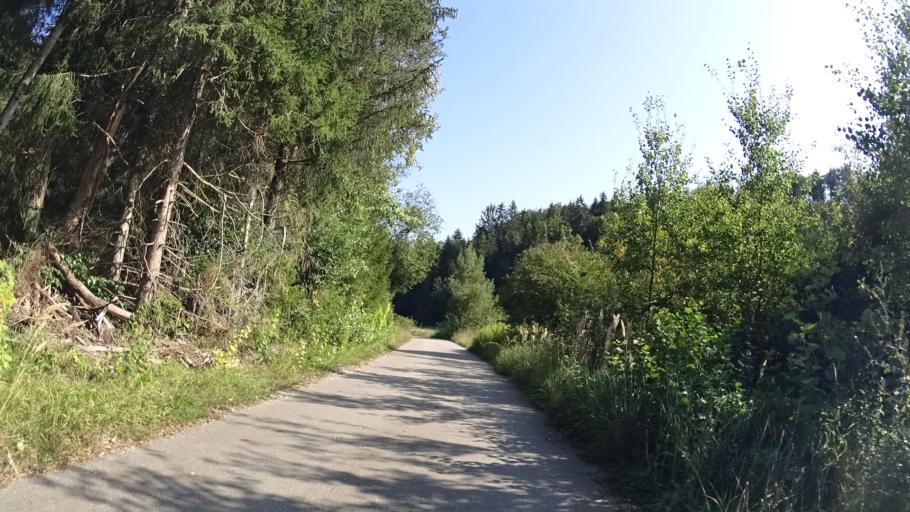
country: DE
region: Bavaria
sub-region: Upper Bavaria
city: Walting
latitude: 48.9082
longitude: 11.2921
